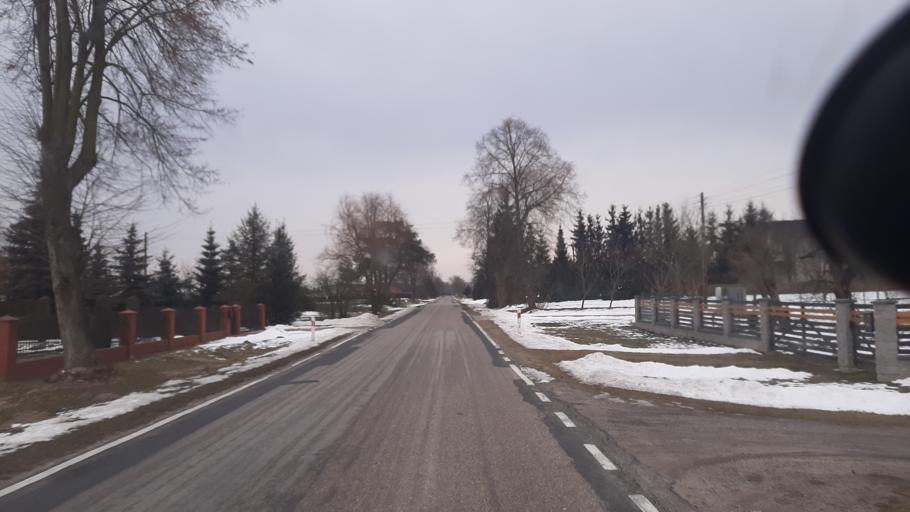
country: PL
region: Lublin Voivodeship
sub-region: Powiat lubartowski
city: Kamionka
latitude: 51.4580
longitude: 22.4207
